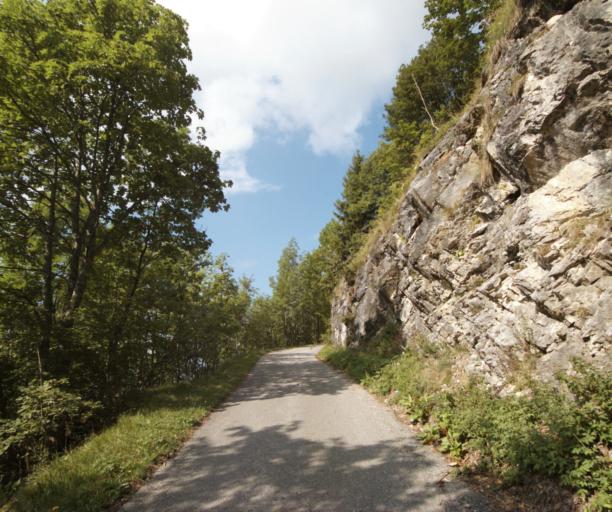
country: CH
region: Vaud
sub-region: Riviera-Pays-d'Enhaut District
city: Caux
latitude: 46.4233
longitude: 6.9834
